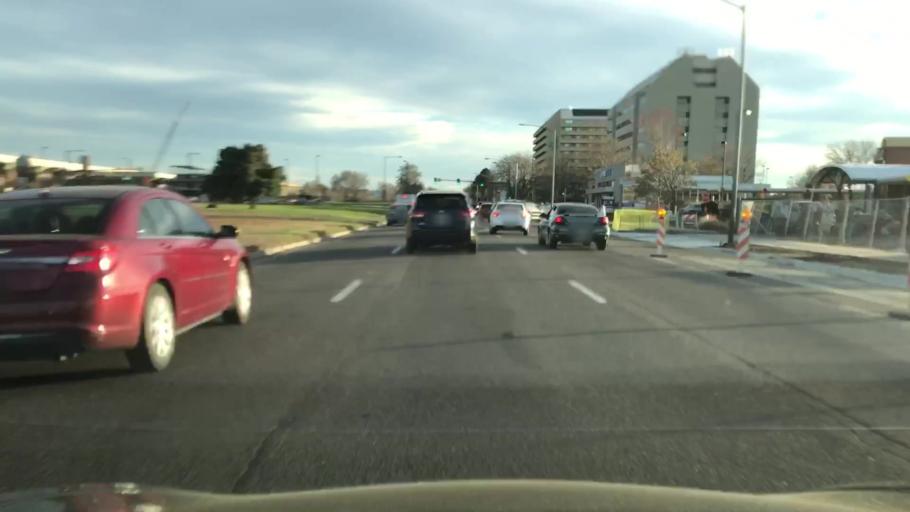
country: US
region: Colorado
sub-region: Adams County
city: Commerce City
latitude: 39.7673
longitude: -104.9035
